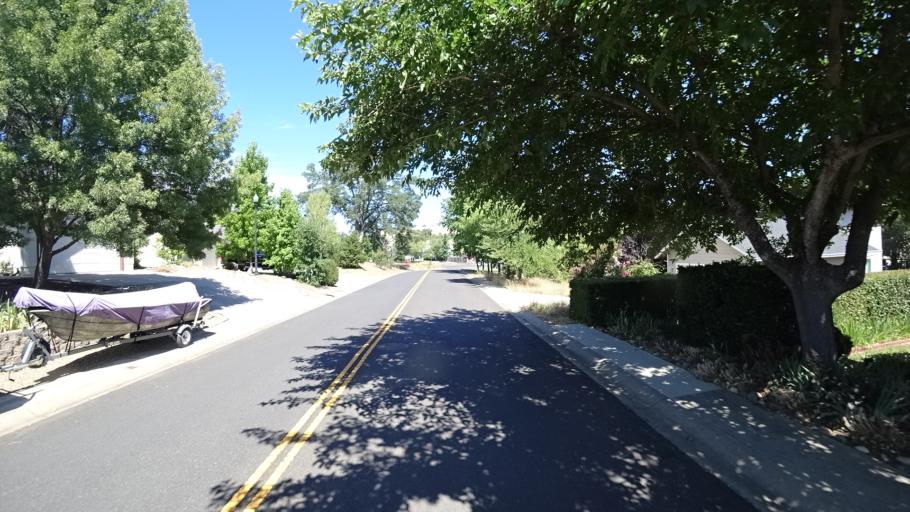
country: US
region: California
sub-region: Calaveras County
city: Angels Camp
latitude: 38.0754
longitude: -120.5384
